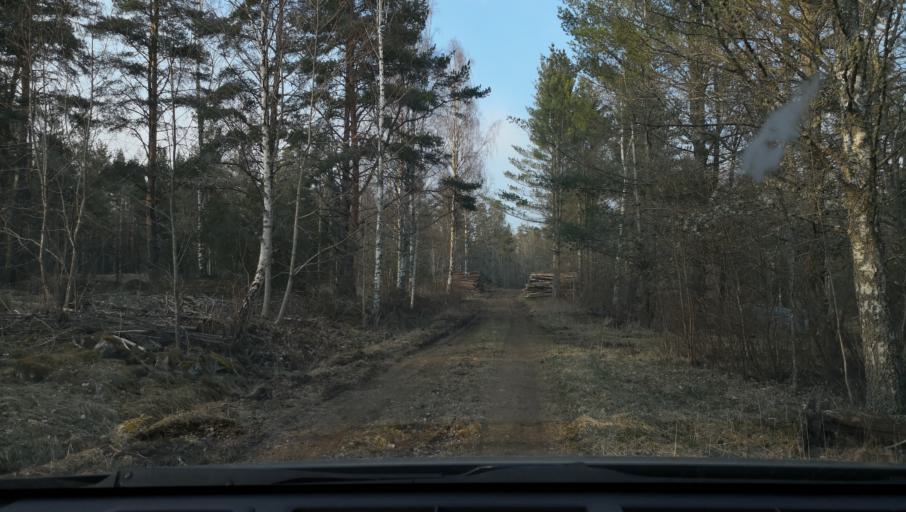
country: SE
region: OErebro
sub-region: Orebro Kommun
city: Hovsta
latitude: 59.3901
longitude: 15.2659
